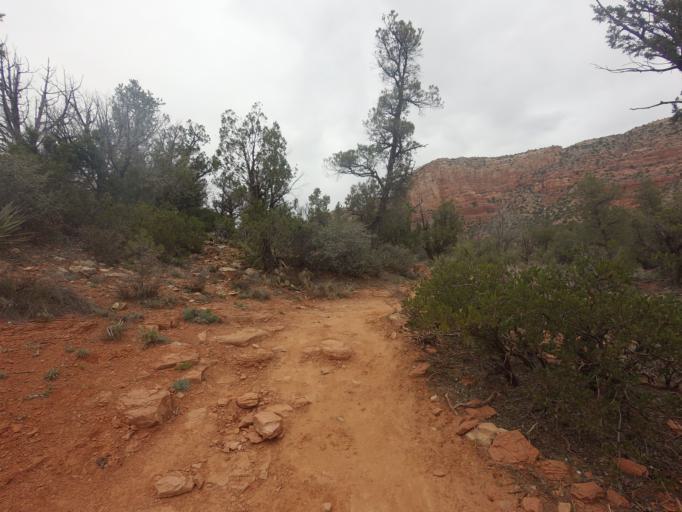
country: US
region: Arizona
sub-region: Yavapai County
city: Village of Oak Creek (Big Park)
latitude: 34.8012
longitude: -111.7469
